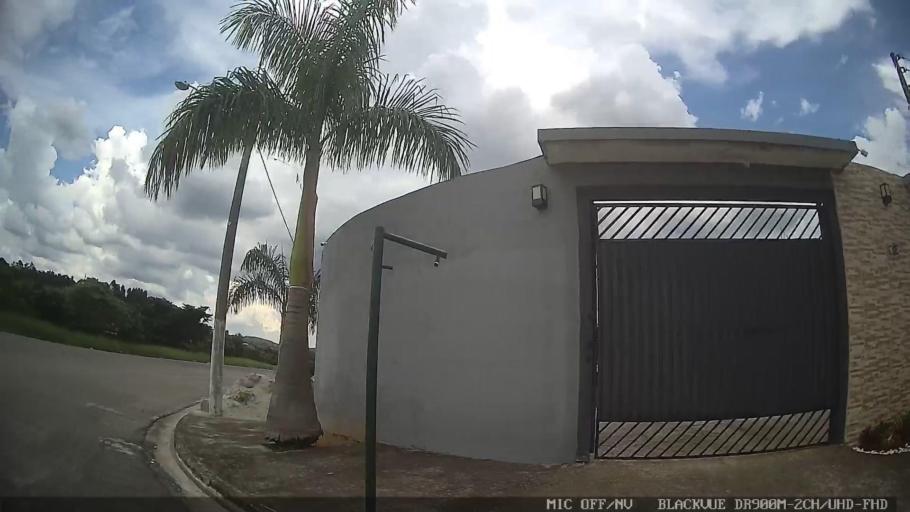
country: BR
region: Sao Paulo
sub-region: Atibaia
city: Atibaia
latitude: -23.1286
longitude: -46.5995
